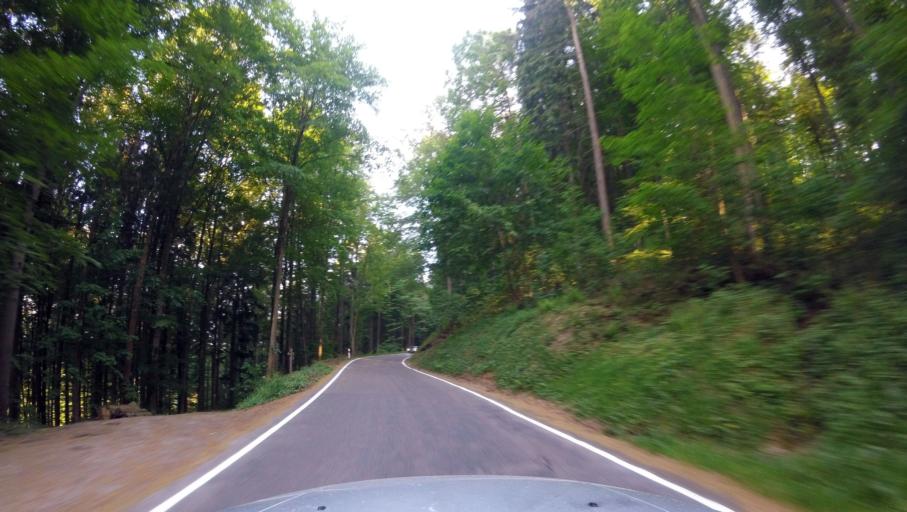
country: DE
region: Baden-Wuerttemberg
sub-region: Regierungsbezirk Stuttgart
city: Spiegelberg
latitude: 49.0343
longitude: 9.4436
